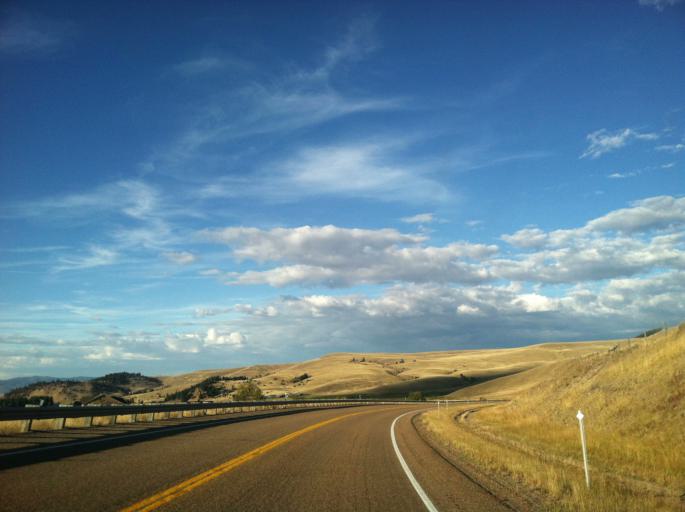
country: US
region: Montana
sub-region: Granite County
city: Philipsburg
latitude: 46.4884
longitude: -113.2303
